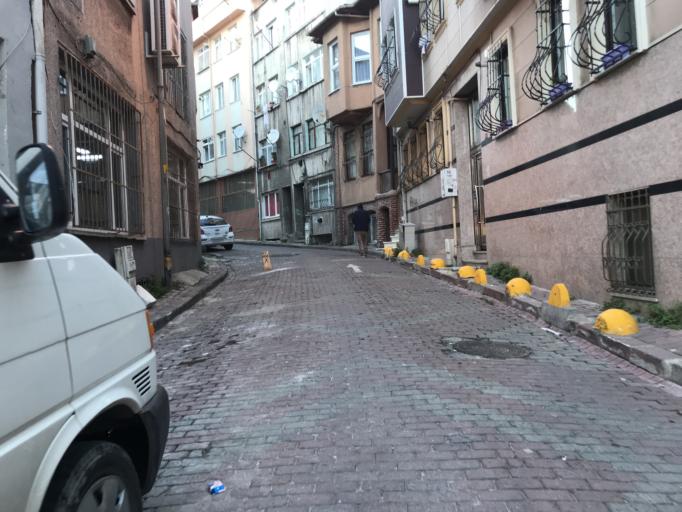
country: TR
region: Istanbul
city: Istanbul
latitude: 41.0279
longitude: 28.9549
